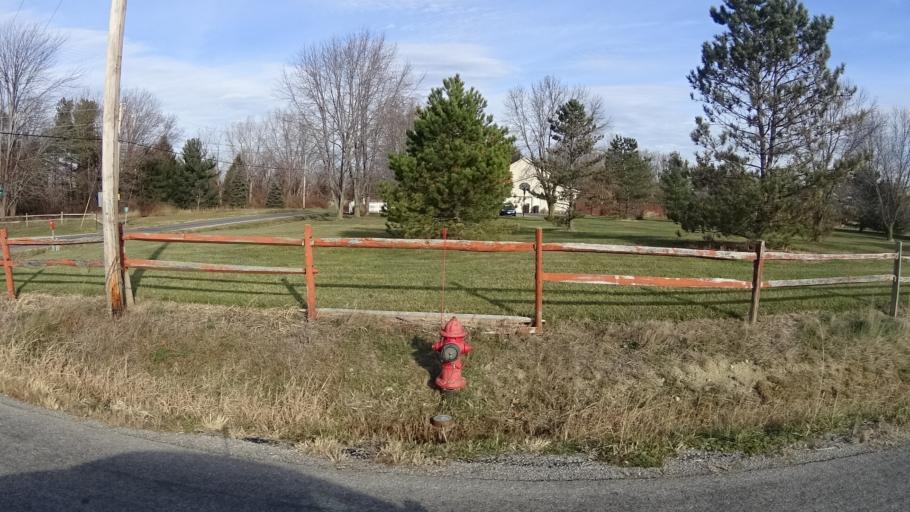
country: US
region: Ohio
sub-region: Lorain County
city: Grafton
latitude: 41.2228
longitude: -82.0624
